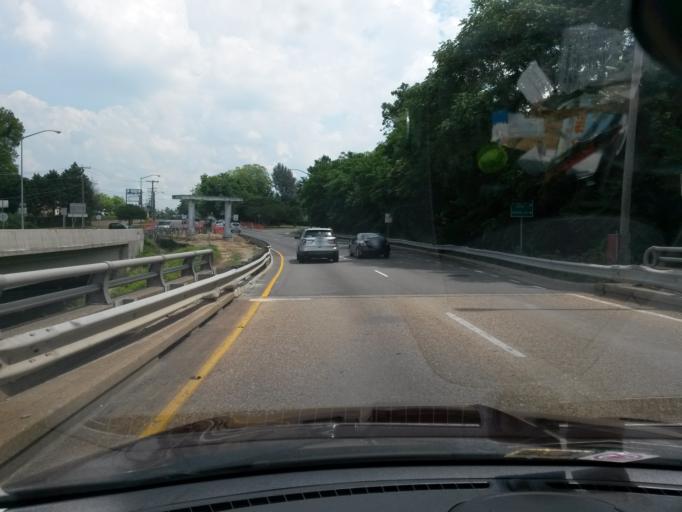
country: US
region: Virginia
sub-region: City of Hopewell
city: Hopewell
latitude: 37.3101
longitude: -77.2964
